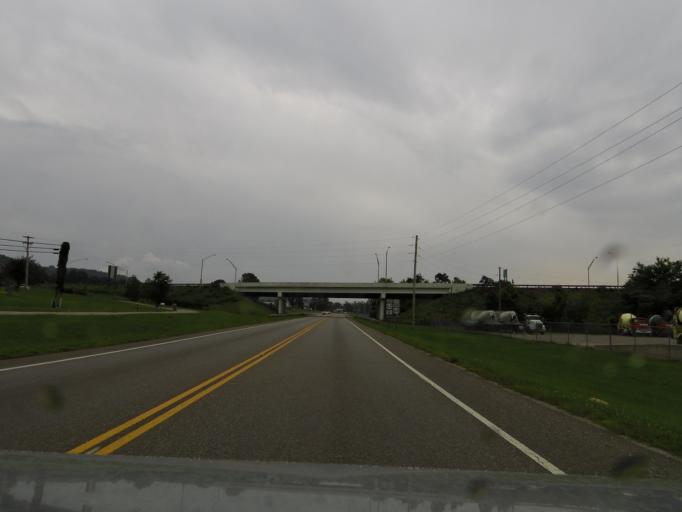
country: US
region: Ohio
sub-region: Brown County
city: Aberdeen
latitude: 38.6875
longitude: -83.7775
